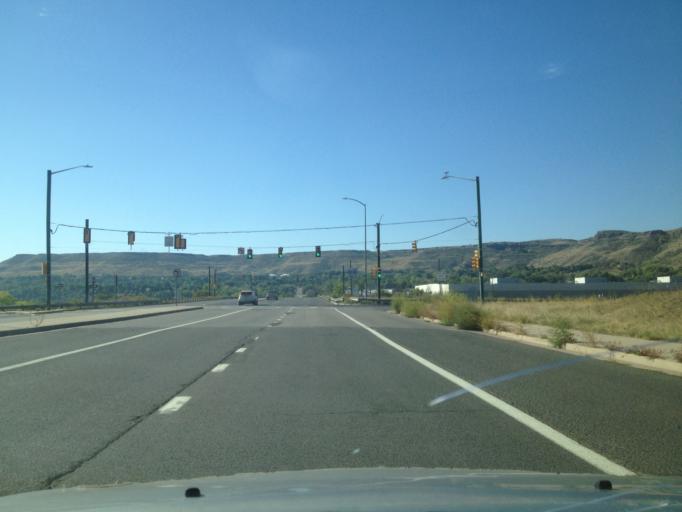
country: US
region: Colorado
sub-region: Jefferson County
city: Applewood
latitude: 39.7742
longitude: -105.1748
